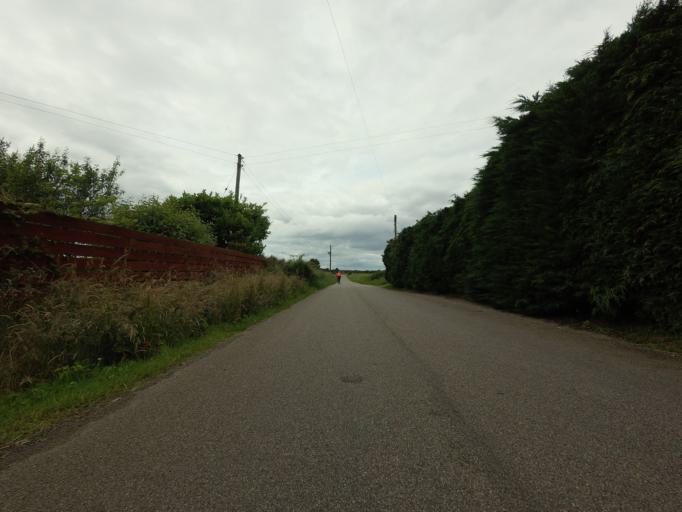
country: GB
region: Scotland
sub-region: Moray
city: Forres
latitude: 57.6037
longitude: -3.7267
